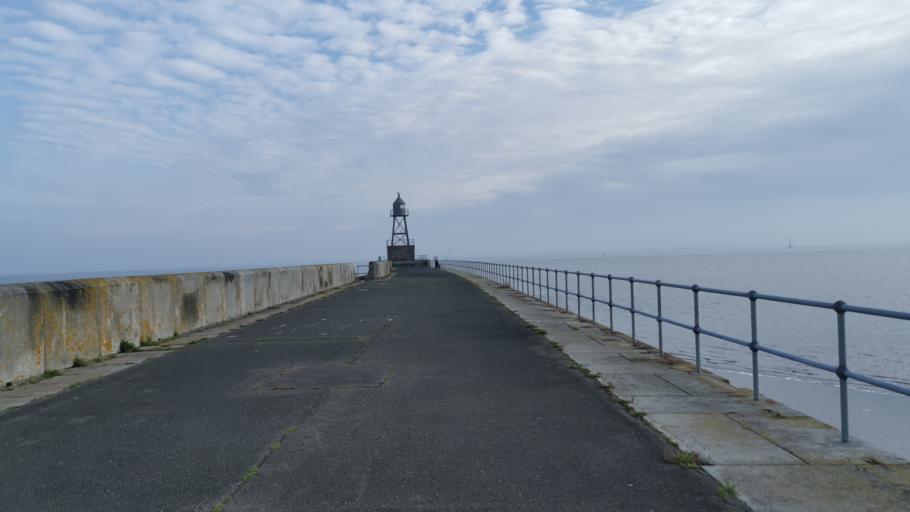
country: DE
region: Lower Saxony
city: Wilhelmshaven
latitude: 53.5201
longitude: 8.1628
